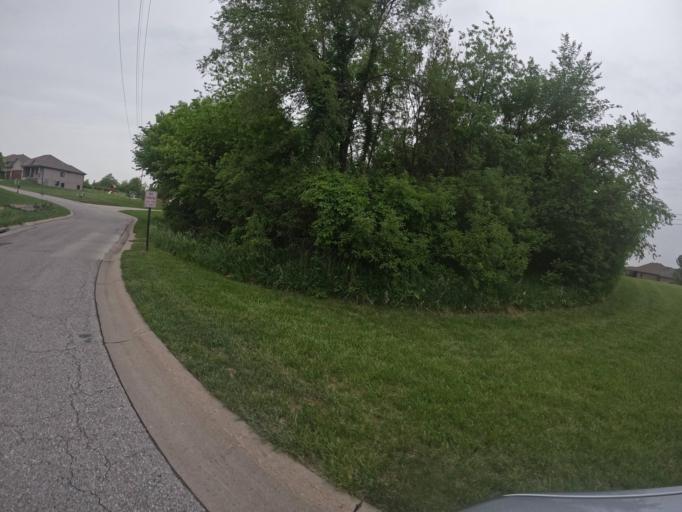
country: US
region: Nebraska
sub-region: Sarpy County
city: Offutt Air Force Base
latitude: 41.0469
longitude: -95.9610
